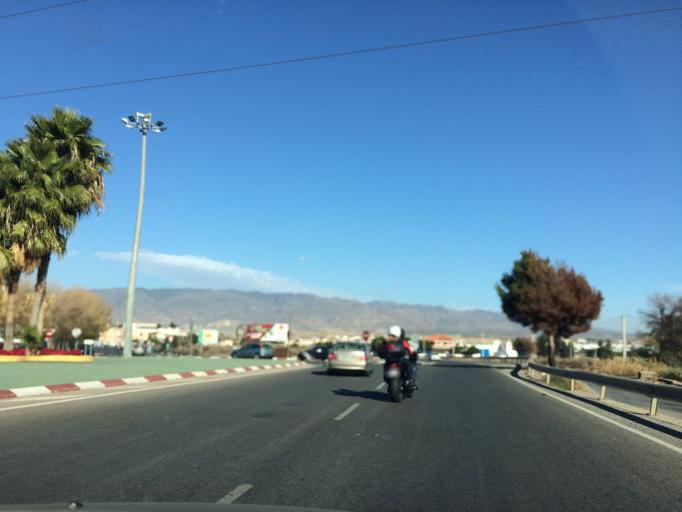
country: ES
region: Andalusia
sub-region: Provincia de Almeria
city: Huercal de Almeria
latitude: 36.8727
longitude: -2.4410
